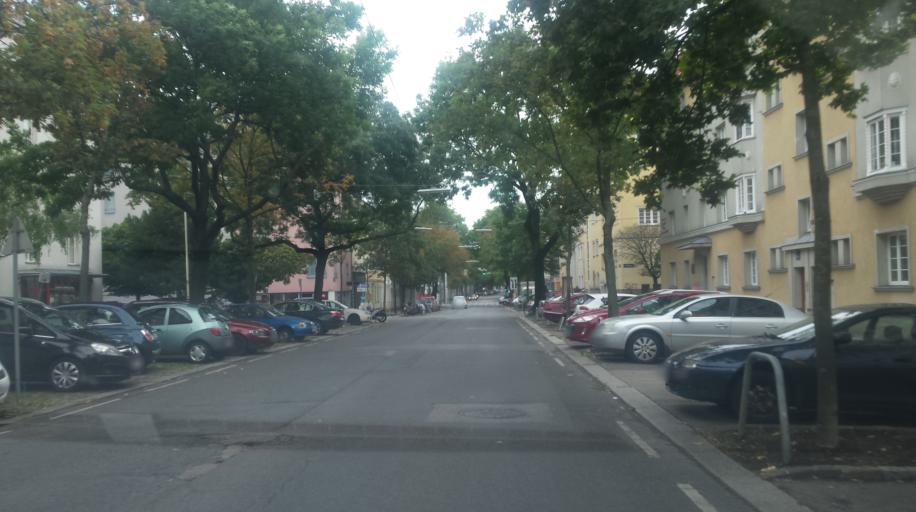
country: AT
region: Vienna
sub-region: Wien Stadt
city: Vienna
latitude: 48.1734
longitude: 16.4123
